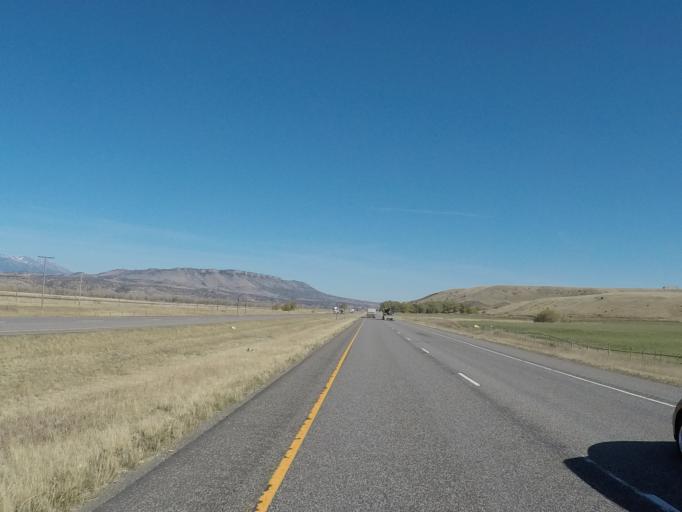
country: US
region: Montana
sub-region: Park County
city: Livingston
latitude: 45.6992
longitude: -110.4738
